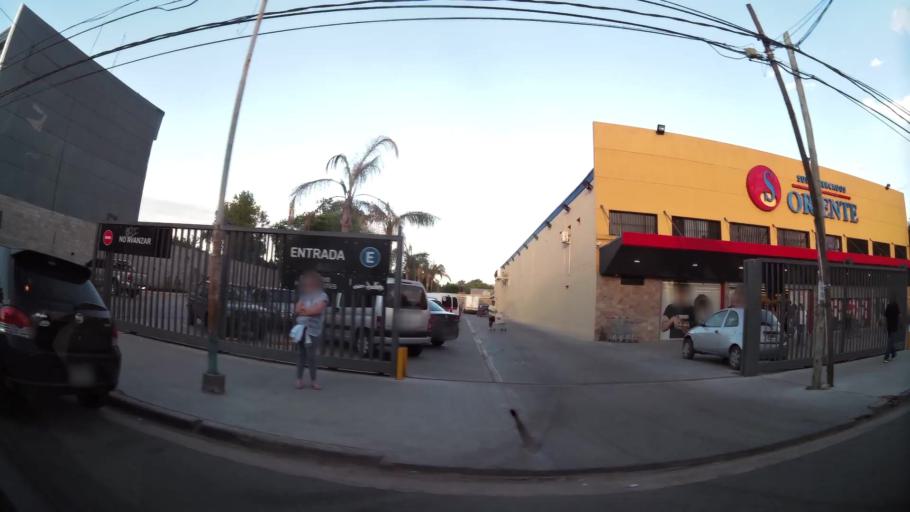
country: AR
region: Buenos Aires
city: Santa Catalina - Dique Lujan
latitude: -34.4682
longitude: -58.7570
